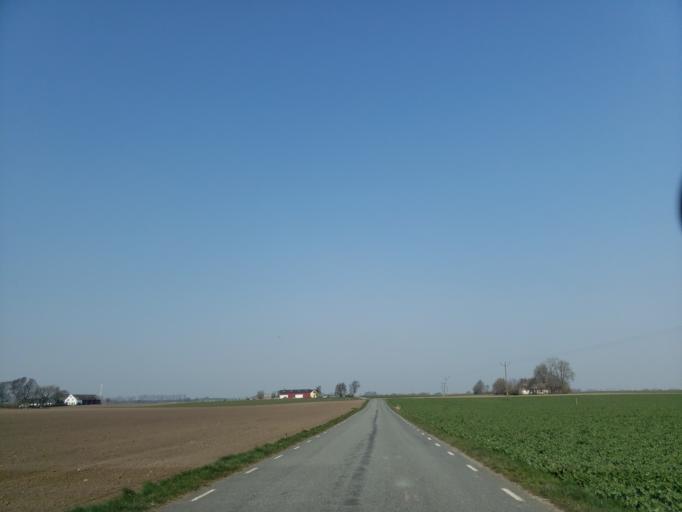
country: SE
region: Skane
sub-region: Simrishamns Kommun
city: Simrishamn
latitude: 55.4538
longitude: 14.2147
